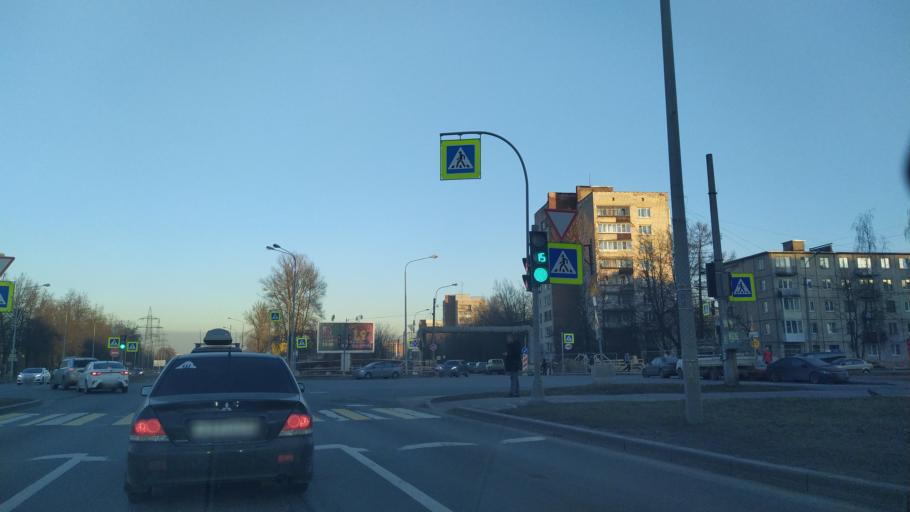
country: RU
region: Leningrad
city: Kalininskiy
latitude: 59.9769
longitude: 30.4013
